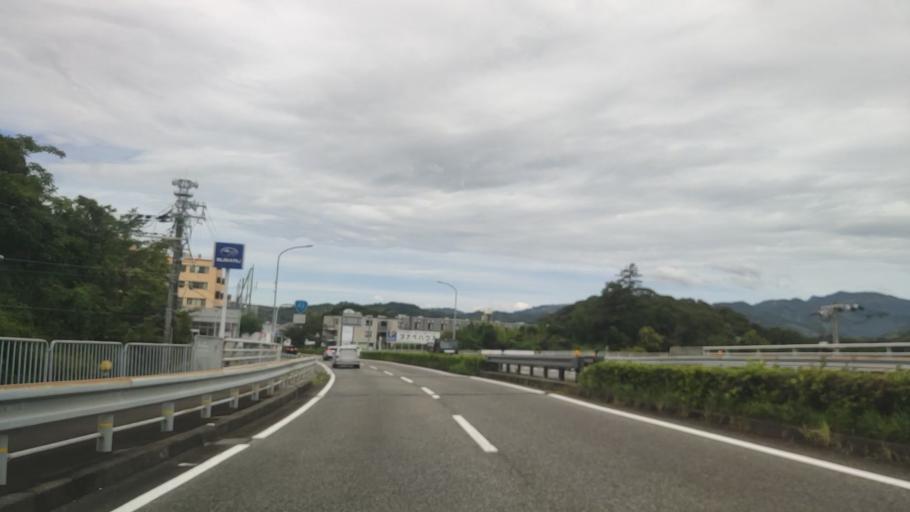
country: JP
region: Wakayama
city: Tanabe
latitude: 33.7352
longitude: 135.4000
